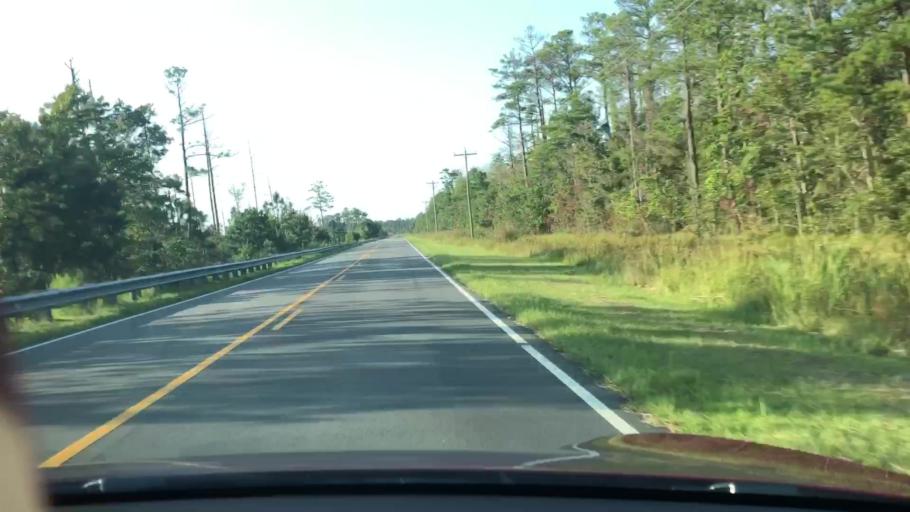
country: US
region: North Carolina
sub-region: Dare County
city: Manteo
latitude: 35.8327
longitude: -75.8105
